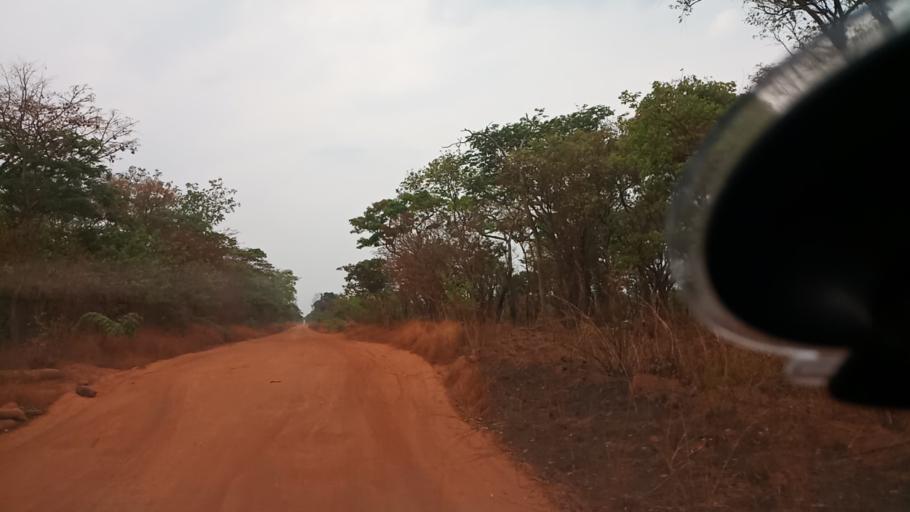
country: ZM
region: Luapula
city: Nchelenge
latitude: -9.4904
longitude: 28.2288
